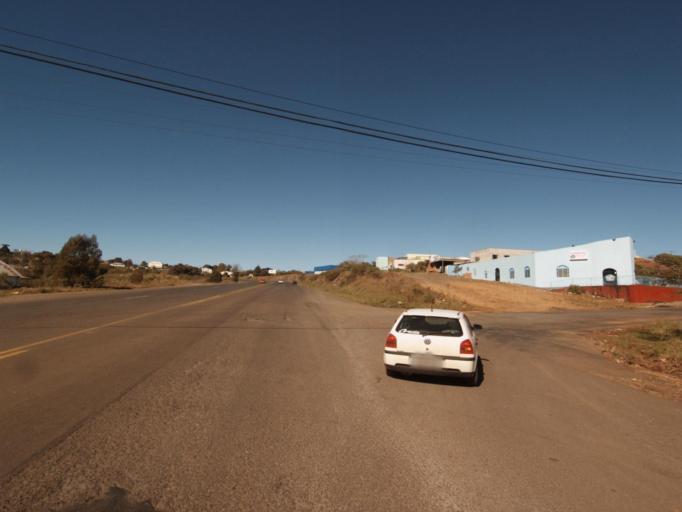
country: BR
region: Santa Catarina
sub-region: Xanxere
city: Xanxere
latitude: -26.8846
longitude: -52.4004
